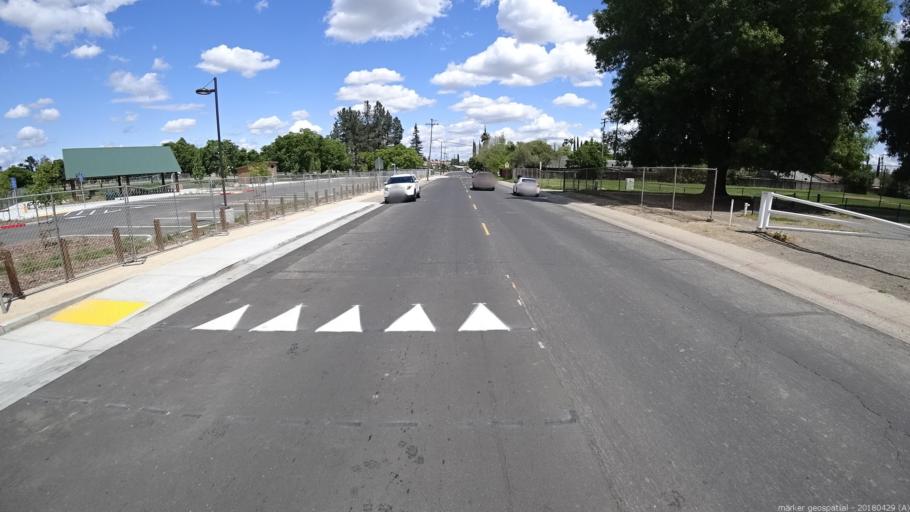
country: US
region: California
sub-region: Yolo County
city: West Sacramento
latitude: 38.5991
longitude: -121.5325
